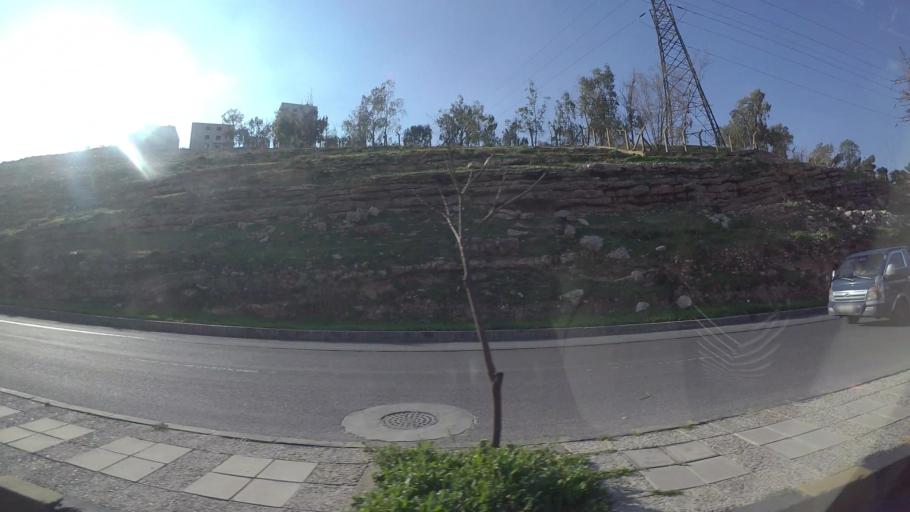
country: JO
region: Amman
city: Amman
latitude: 31.9777
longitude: 35.9711
